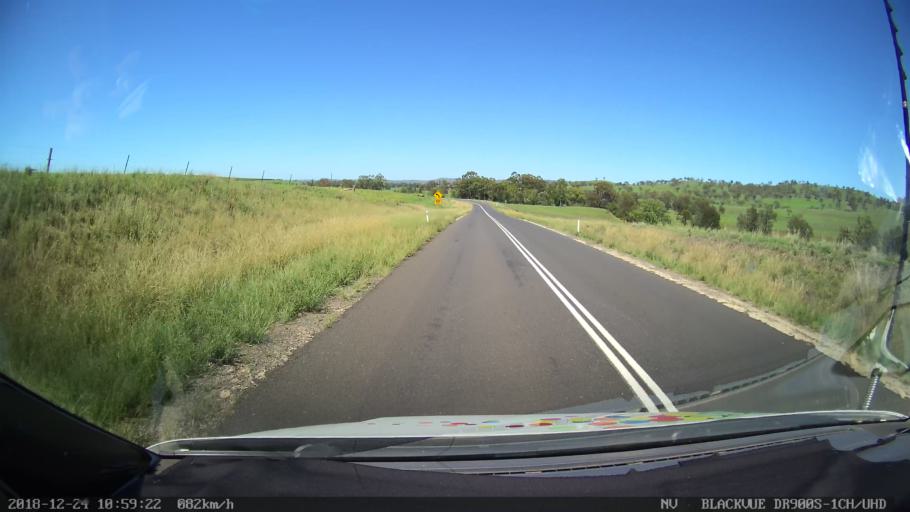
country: AU
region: New South Wales
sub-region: Upper Hunter Shire
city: Merriwa
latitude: -32.0638
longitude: 150.3937
